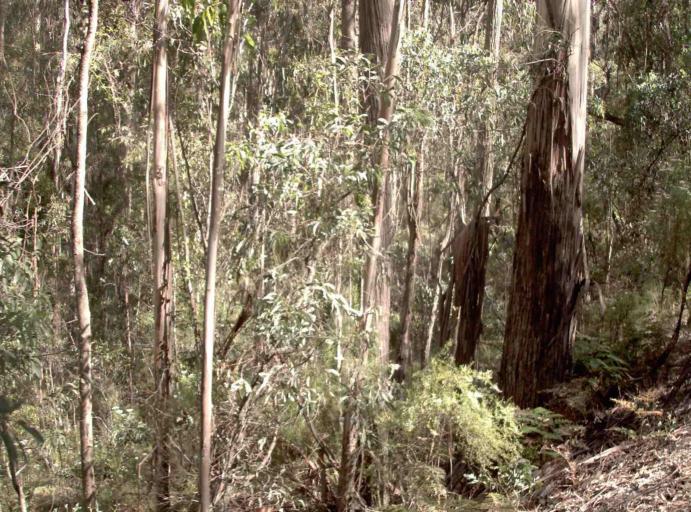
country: AU
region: New South Wales
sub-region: Bombala
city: Bombala
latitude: -37.2893
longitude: 148.7134
